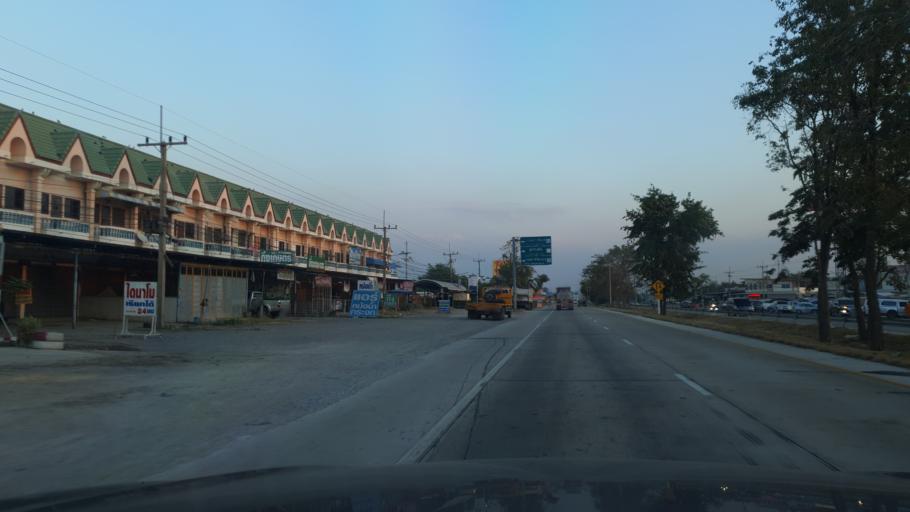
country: TH
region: Nakhon Sawan
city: Kao Liao
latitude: 15.7727
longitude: 99.9831
